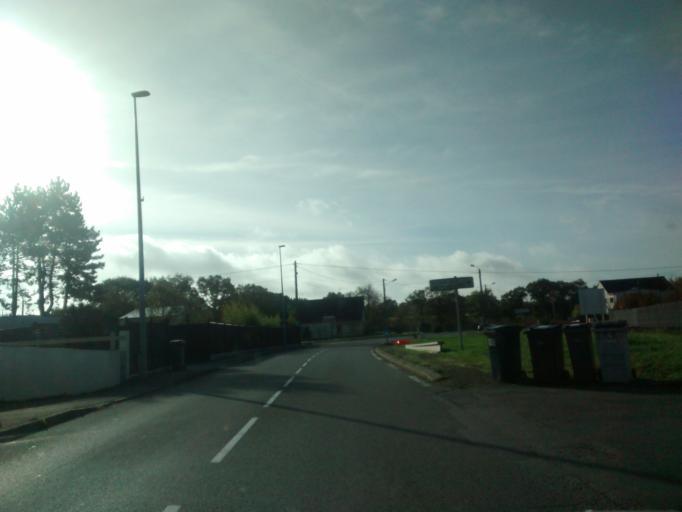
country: FR
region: Brittany
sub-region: Departement d'Ille-et-Vilaine
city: Chantepie
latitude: 48.1003
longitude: -1.6050
